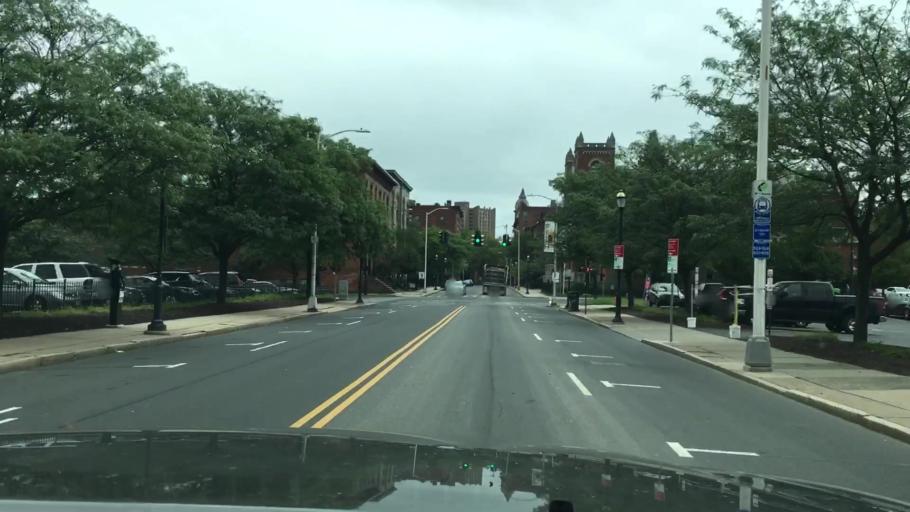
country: US
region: Connecticut
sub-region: Hartford County
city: Hartford
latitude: 41.7616
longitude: -72.6780
